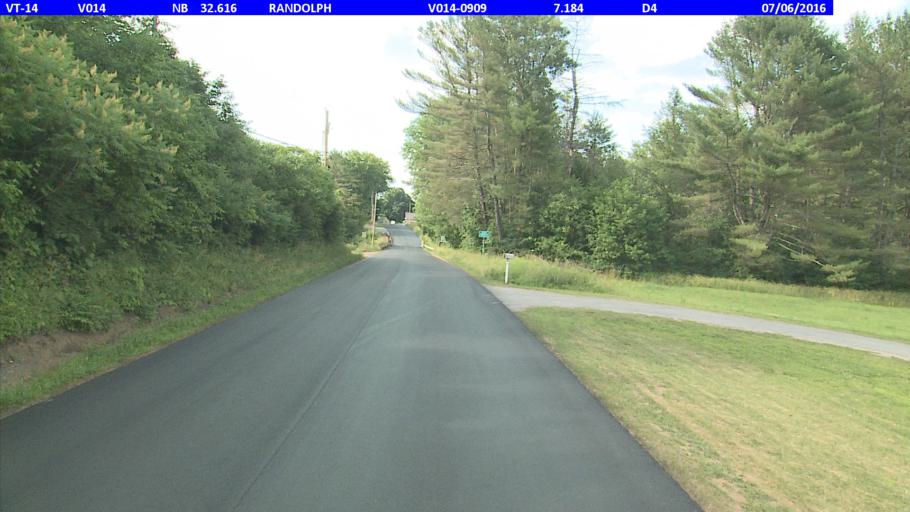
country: US
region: Vermont
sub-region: Orange County
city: Chelsea
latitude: 43.9713
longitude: -72.5545
